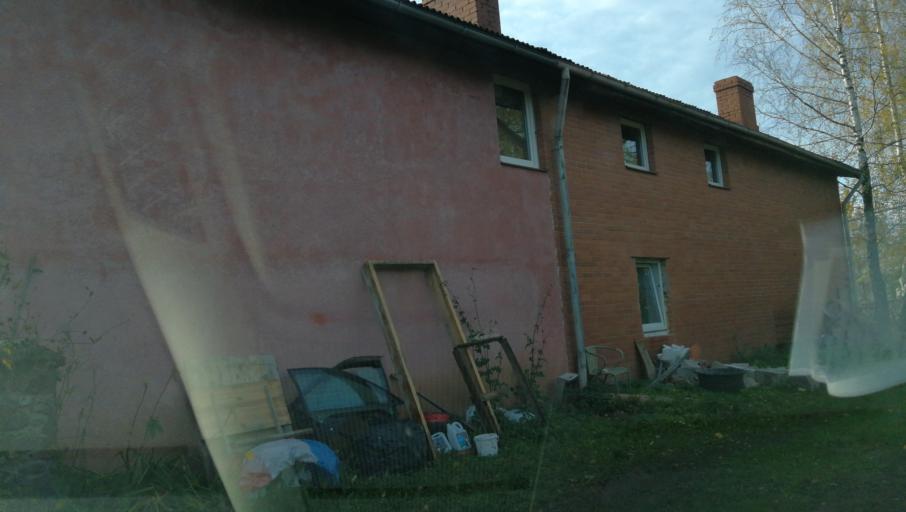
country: LV
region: Cesu Rajons
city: Cesis
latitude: 57.3029
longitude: 25.2530
